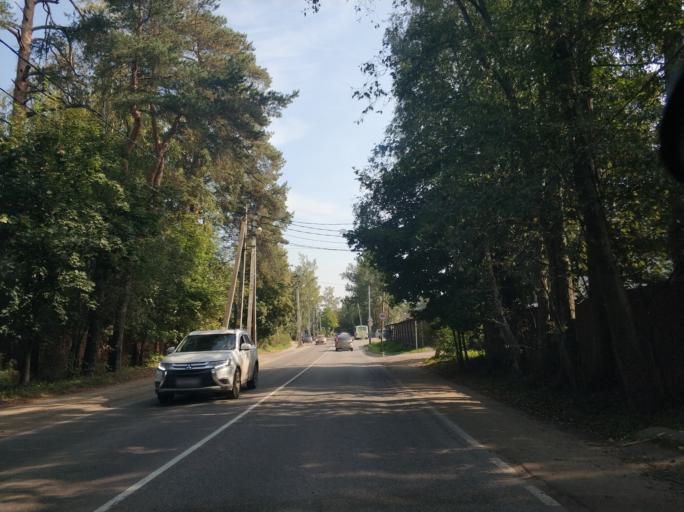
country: RU
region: Leningrad
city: Vsevolozhsk
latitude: 60.0085
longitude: 30.6053
